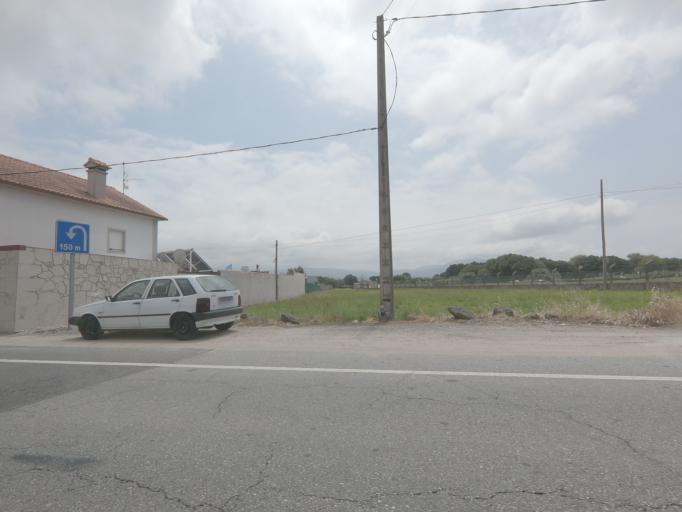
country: ES
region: Galicia
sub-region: Provincia de Pontevedra
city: O Rosal
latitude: 41.9138
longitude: -8.8432
